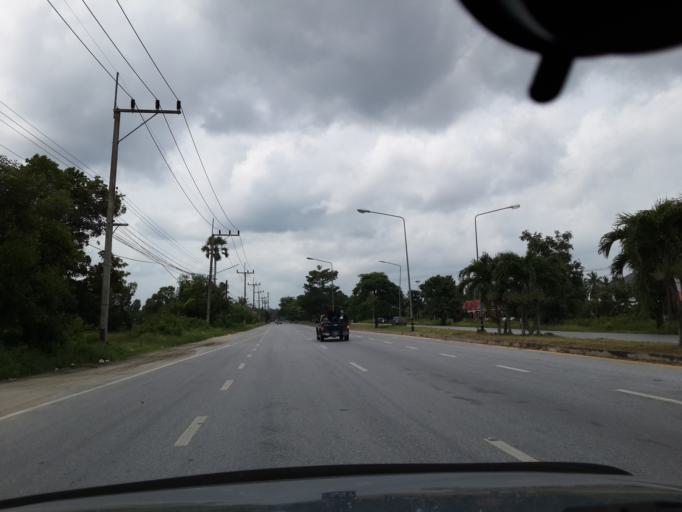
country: TH
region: Pattani
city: Yaring
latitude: 6.8688
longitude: 101.3465
